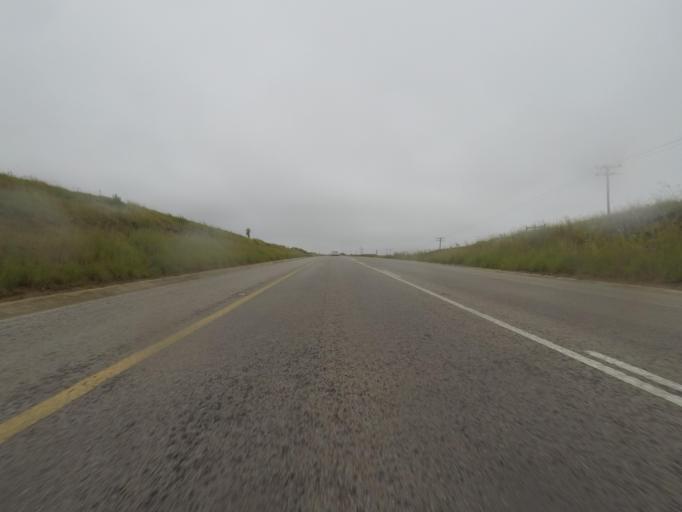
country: ZA
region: Eastern Cape
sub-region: Cacadu District Municipality
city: Grahamstown
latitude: -33.6457
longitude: 26.3801
